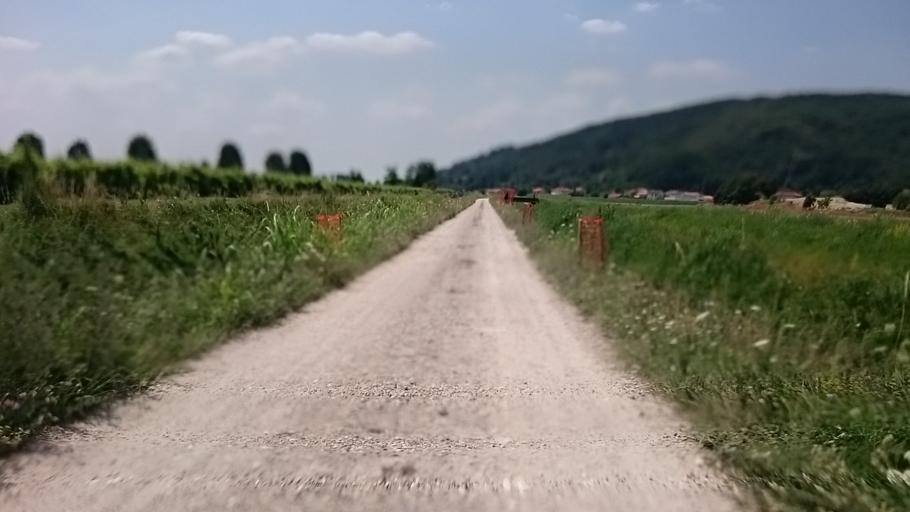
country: IT
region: Veneto
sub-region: Provincia di Padova
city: Montegrotto Terme
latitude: 45.3152
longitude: 11.7945
